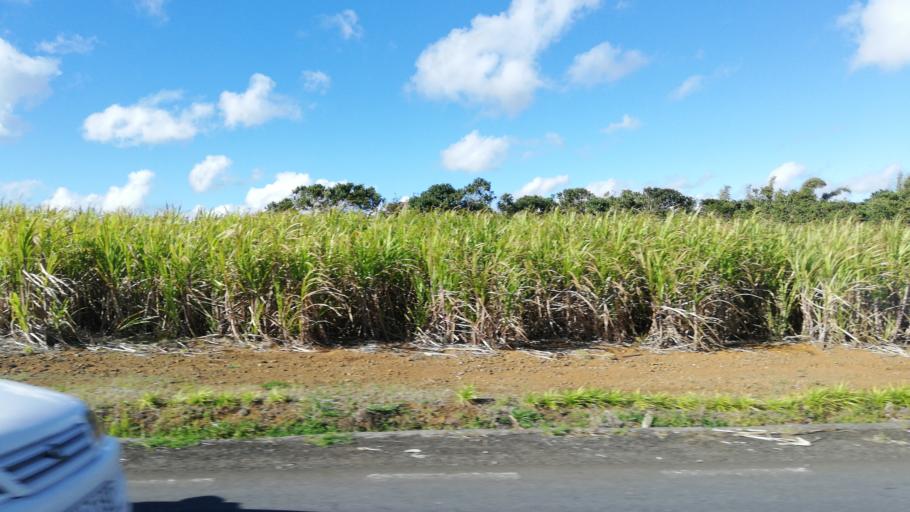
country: MU
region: Moka
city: La Dagotiere
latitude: -20.2321
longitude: 57.5588
